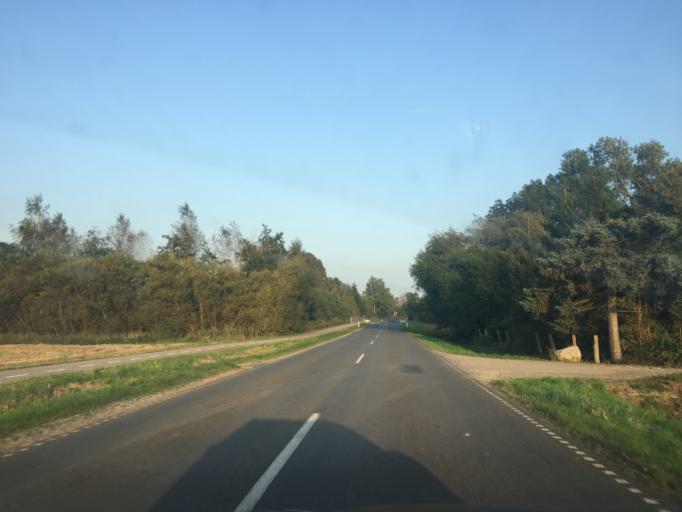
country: DK
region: Zealand
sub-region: Soro Kommune
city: Stenlille
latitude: 55.5434
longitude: 11.6793
